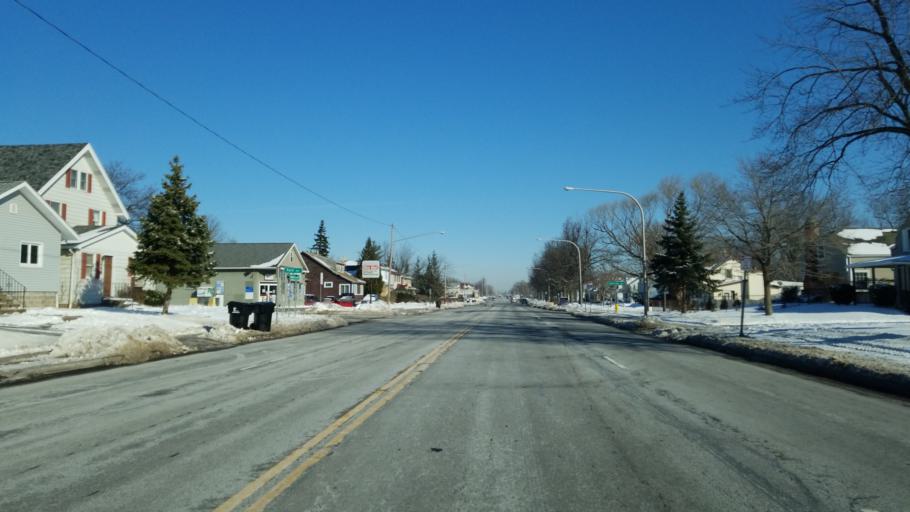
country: US
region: New York
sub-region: Erie County
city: Eggertsville
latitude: 42.9632
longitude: -78.8236
